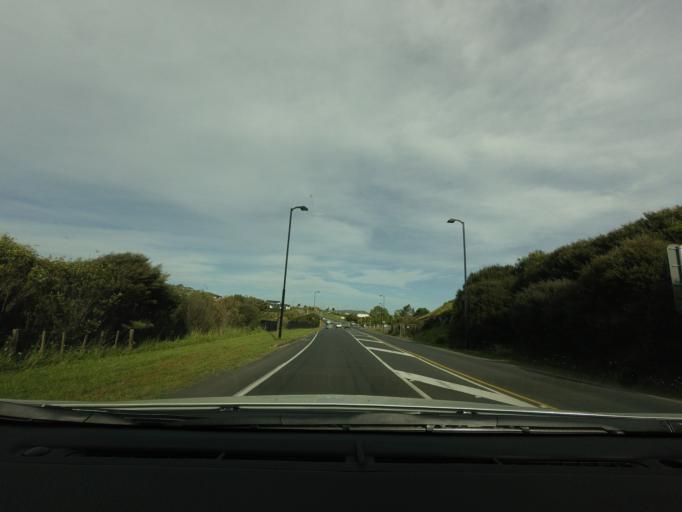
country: NZ
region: Auckland
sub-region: Auckland
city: Rothesay Bay
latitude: -36.5889
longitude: 174.6706
